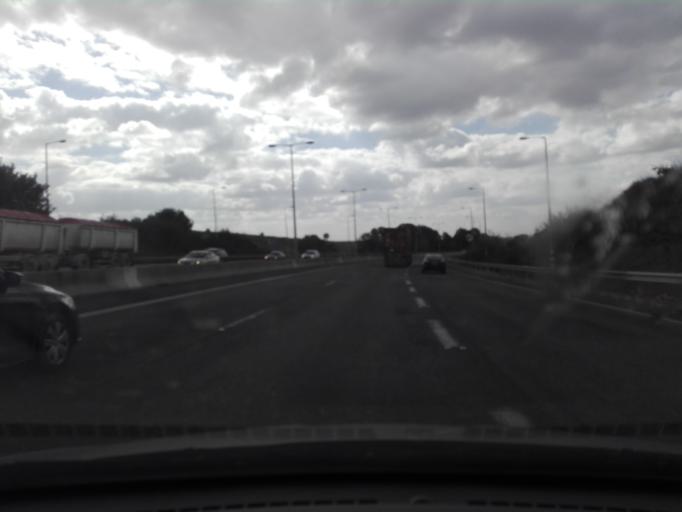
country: IL
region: Haifa
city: Daliyat el Karmil
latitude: 32.6293
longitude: 35.0626
